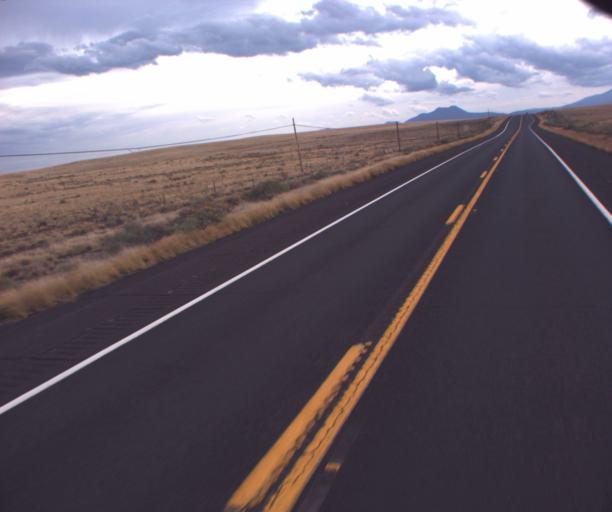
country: US
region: Arizona
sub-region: Coconino County
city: Flagstaff
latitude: 35.6391
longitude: -111.5184
